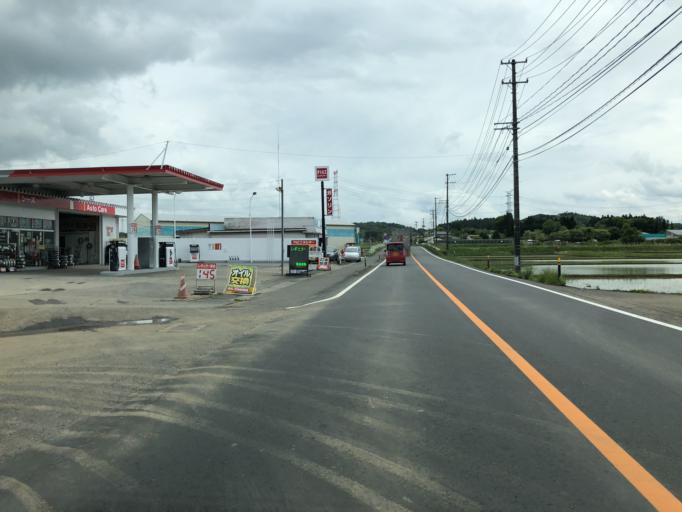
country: JP
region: Fukushima
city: Ishikawa
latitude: 37.0632
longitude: 140.3737
